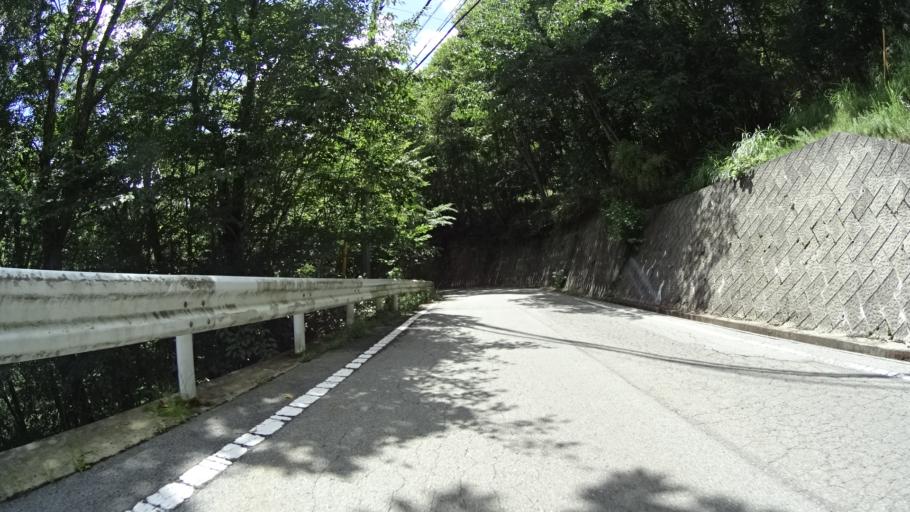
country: JP
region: Yamanashi
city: Enzan
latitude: 35.6866
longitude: 138.8120
